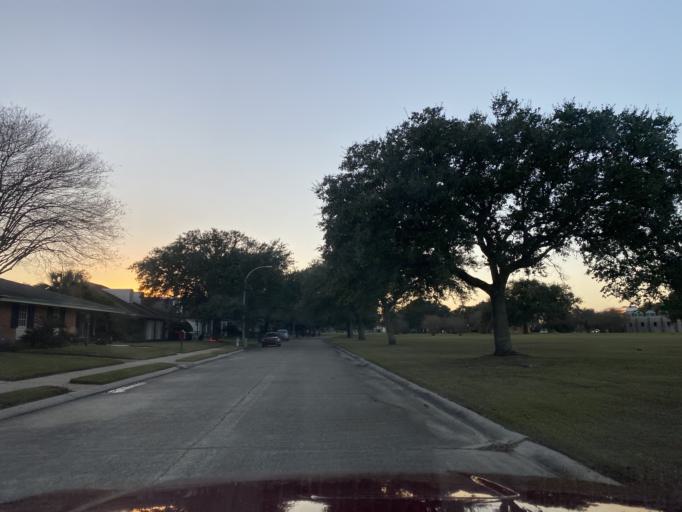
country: US
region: Louisiana
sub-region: Orleans Parish
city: New Orleans
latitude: 30.0294
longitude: -90.0578
